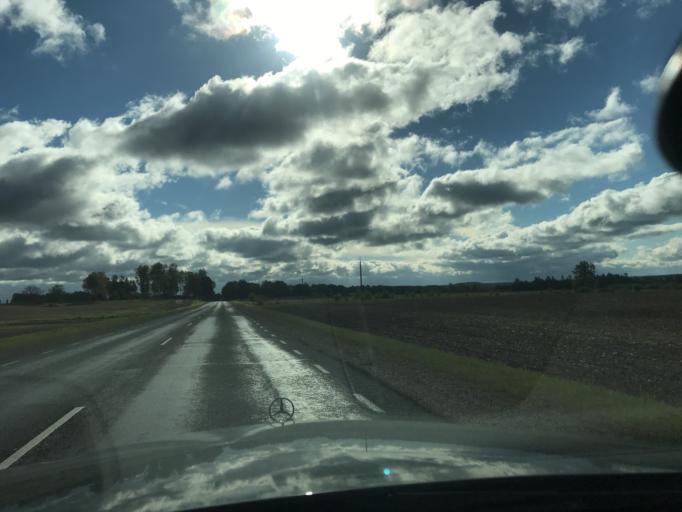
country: EE
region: Vorumaa
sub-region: Antsla vald
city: Vana-Antsla
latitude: 57.9685
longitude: 26.2638
